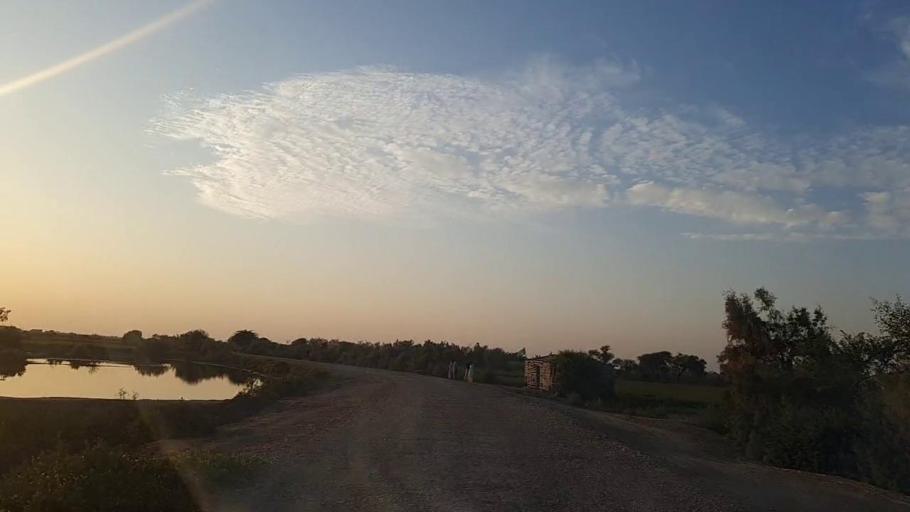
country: PK
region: Sindh
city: Chuhar Jamali
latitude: 24.4610
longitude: 68.1134
